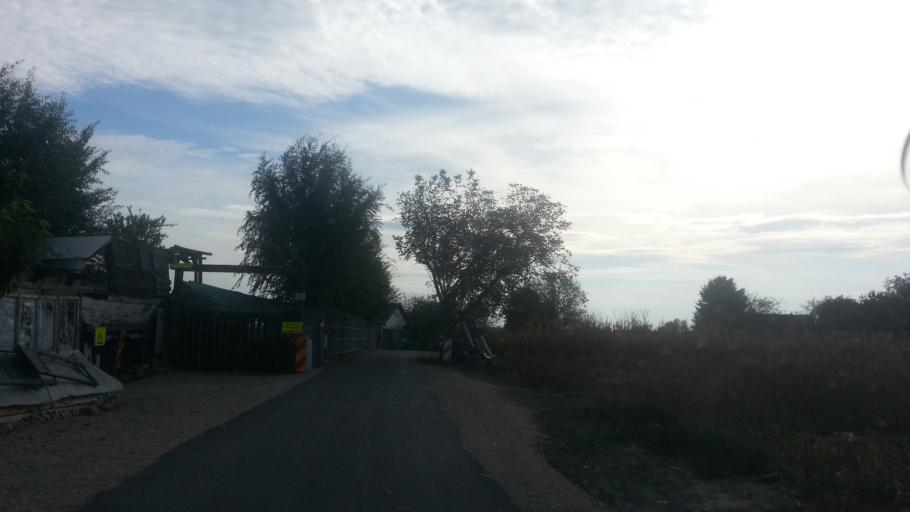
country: RS
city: Belegis
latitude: 45.0217
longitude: 20.3487
